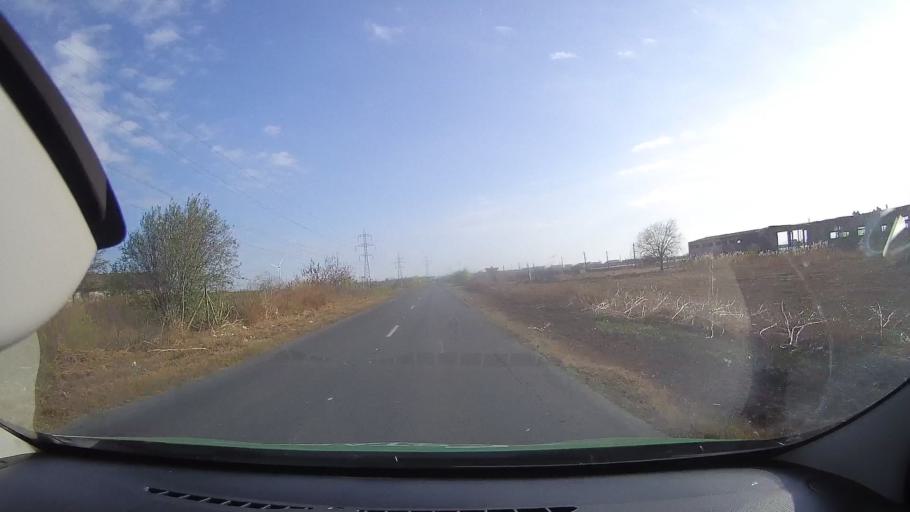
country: RO
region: Constanta
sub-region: Comuna Corbu
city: Corbu
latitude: 44.3693
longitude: 28.6689
